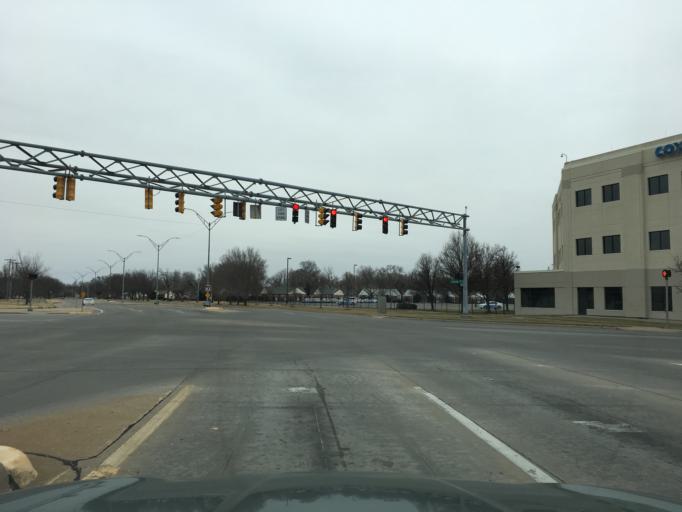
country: US
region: Kansas
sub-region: Sedgwick County
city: Wichita
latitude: 37.6722
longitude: -97.3082
